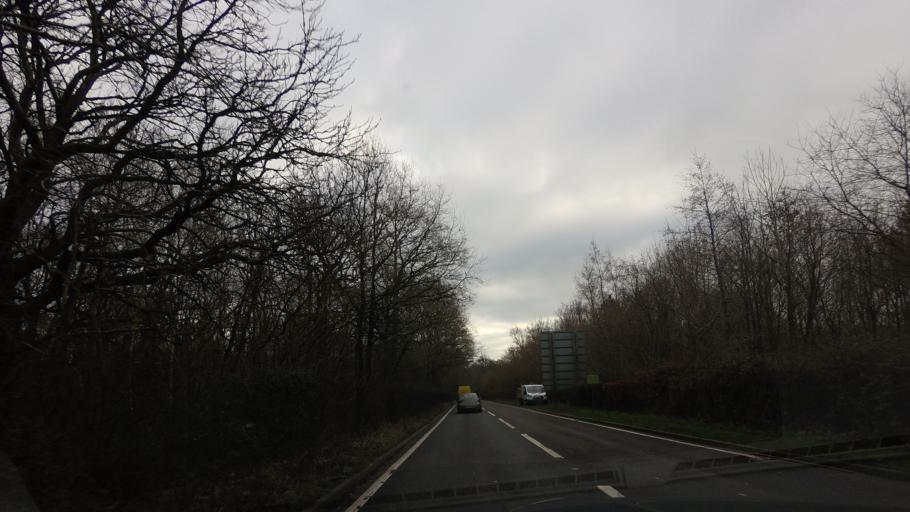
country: GB
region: England
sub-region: East Sussex
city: Wadhurst
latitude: 51.0901
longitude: 0.3969
